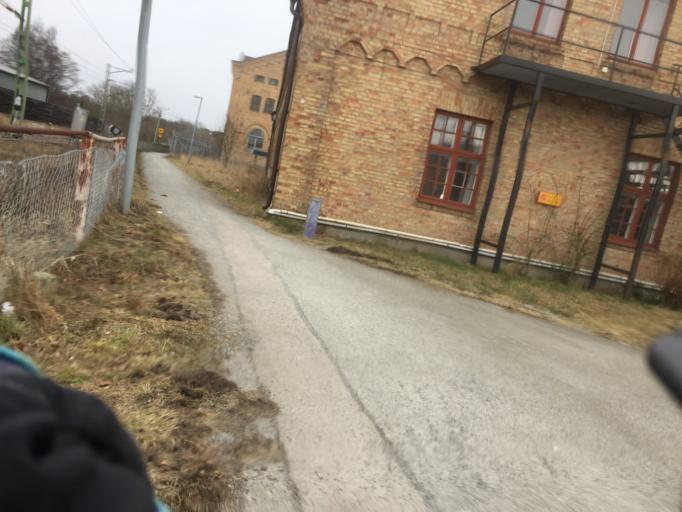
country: SE
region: Blekinge
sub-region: Karlshamns Kommun
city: Morrum
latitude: 56.1867
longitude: 14.7460
